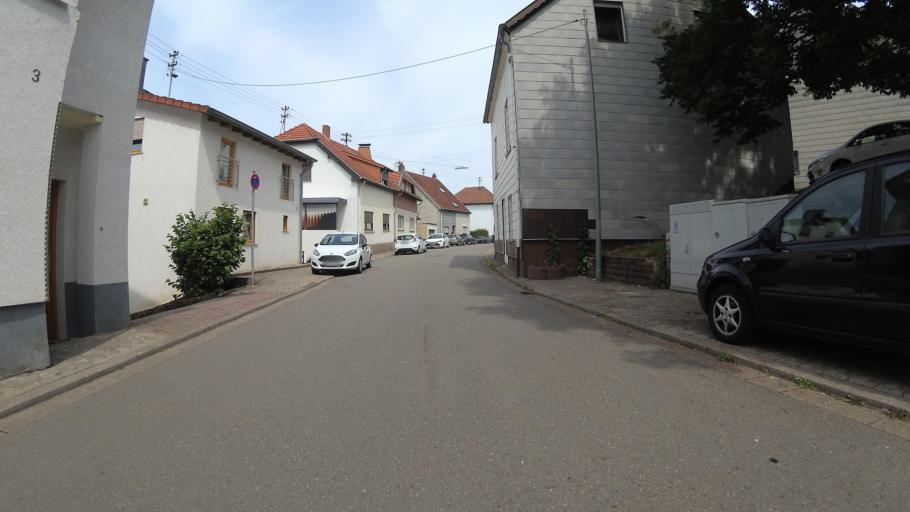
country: DE
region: Saarland
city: Quierschied
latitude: 49.3303
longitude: 7.0560
